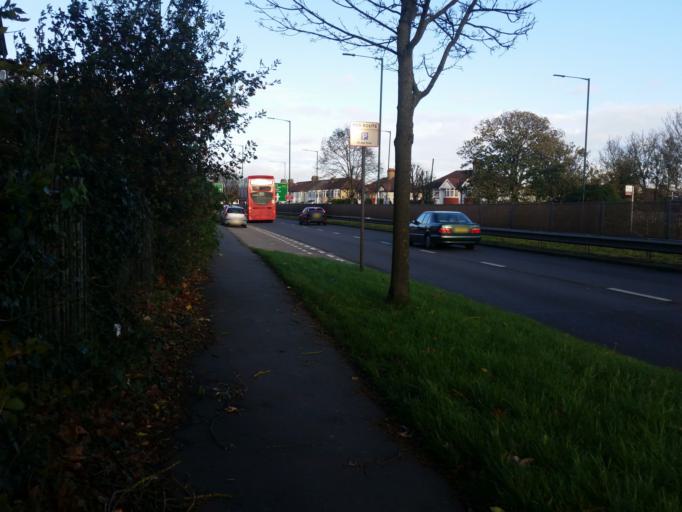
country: GB
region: England
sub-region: Greater London
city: Enfield
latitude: 51.6327
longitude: -0.0723
